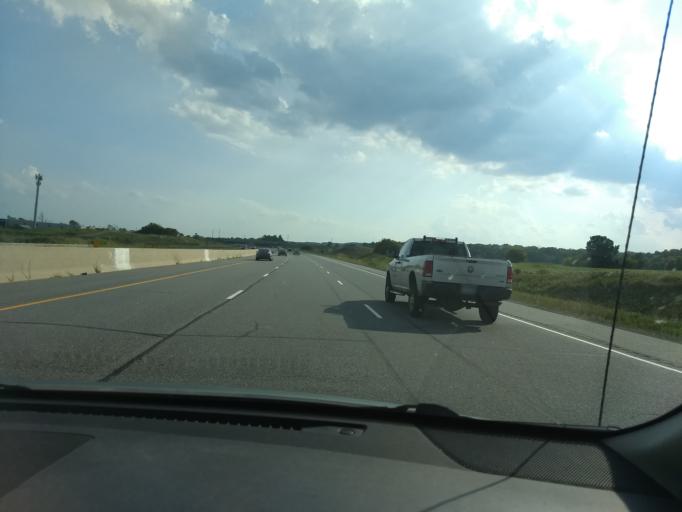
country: CA
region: Ontario
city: Burlington
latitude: 43.4047
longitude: -79.8306
